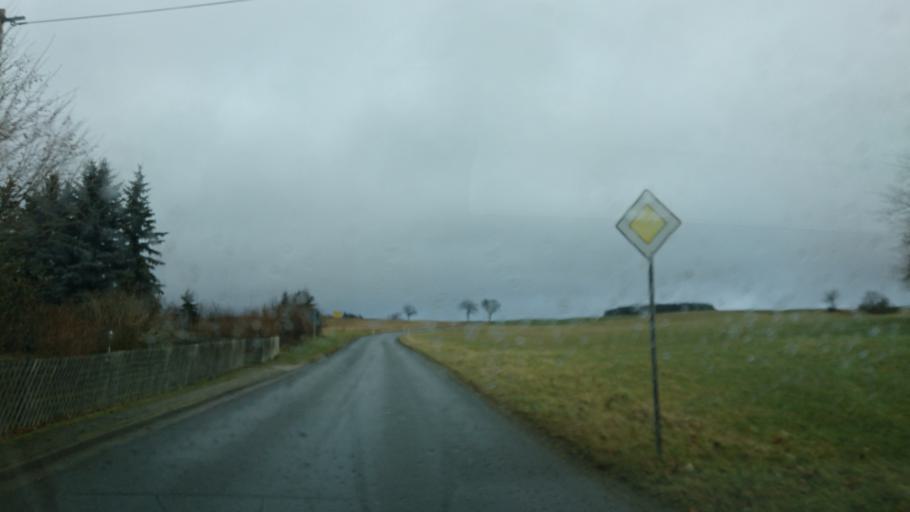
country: DE
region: Thuringia
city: Tanna
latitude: 50.5049
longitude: 11.8644
